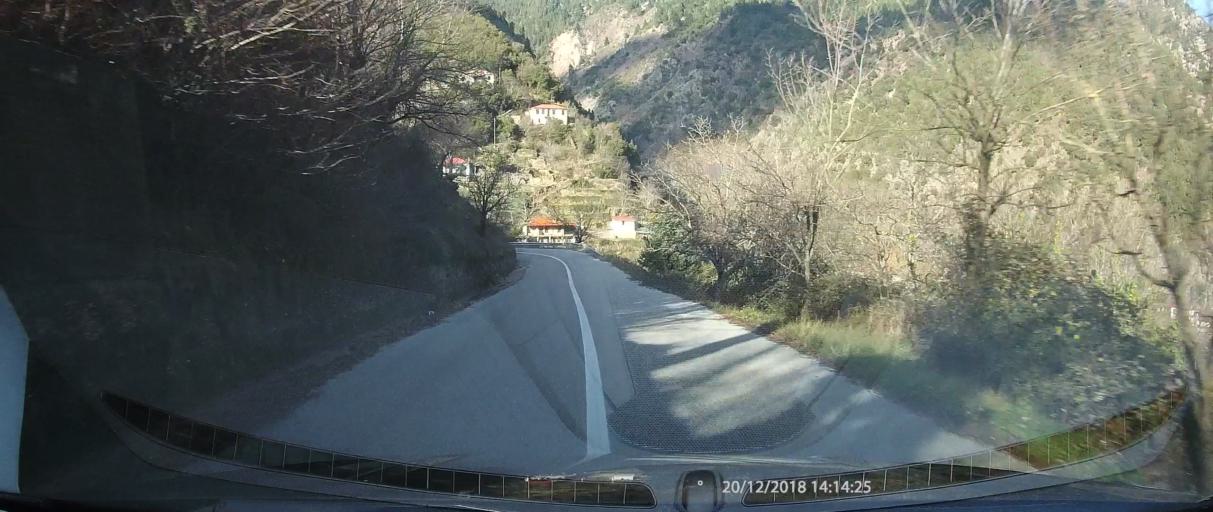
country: GR
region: West Greece
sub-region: Nomos Aitolias kai Akarnanias
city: Thermo
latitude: 38.7473
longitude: 21.6527
